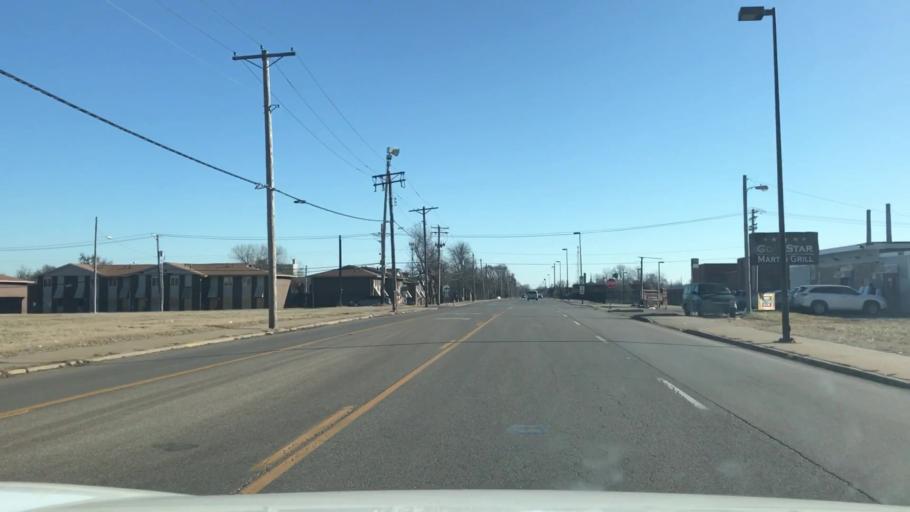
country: US
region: Illinois
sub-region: Saint Clair County
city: East Saint Louis
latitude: 38.6211
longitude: -90.1571
